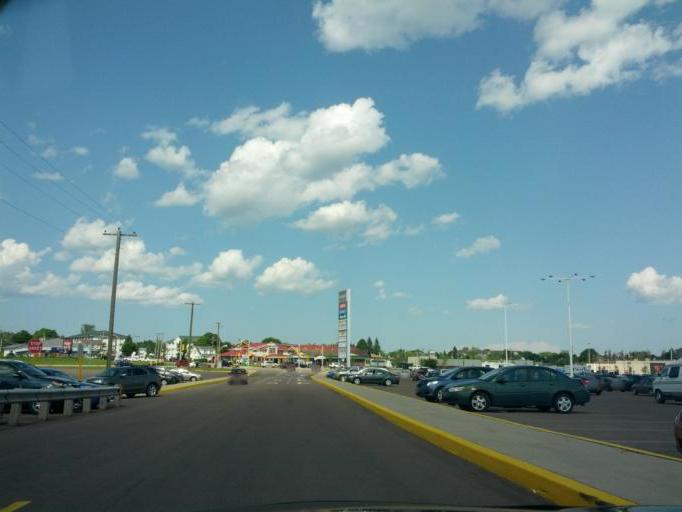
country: CA
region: New Brunswick
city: Moncton
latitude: 46.0980
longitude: -64.7625
